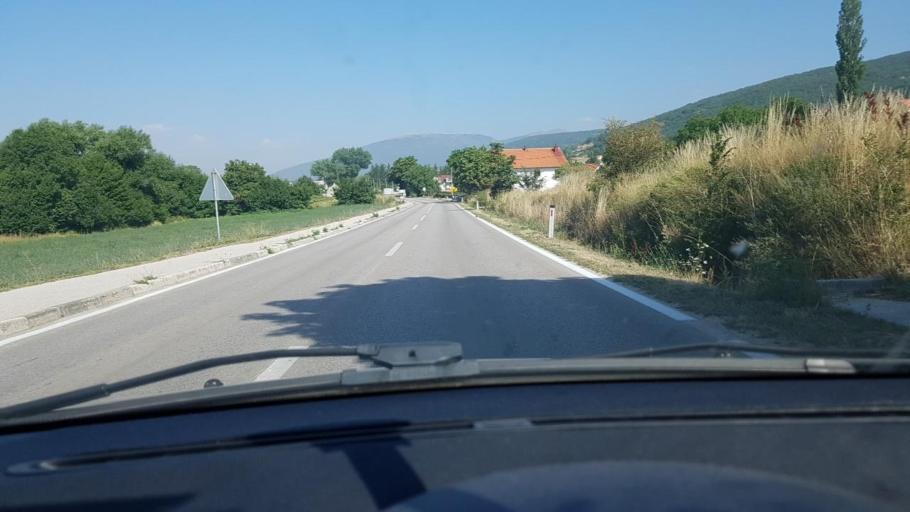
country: BA
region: Federation of Bosnia and Herzegovina
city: Livno
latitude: 43.8352
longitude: 16.9829
